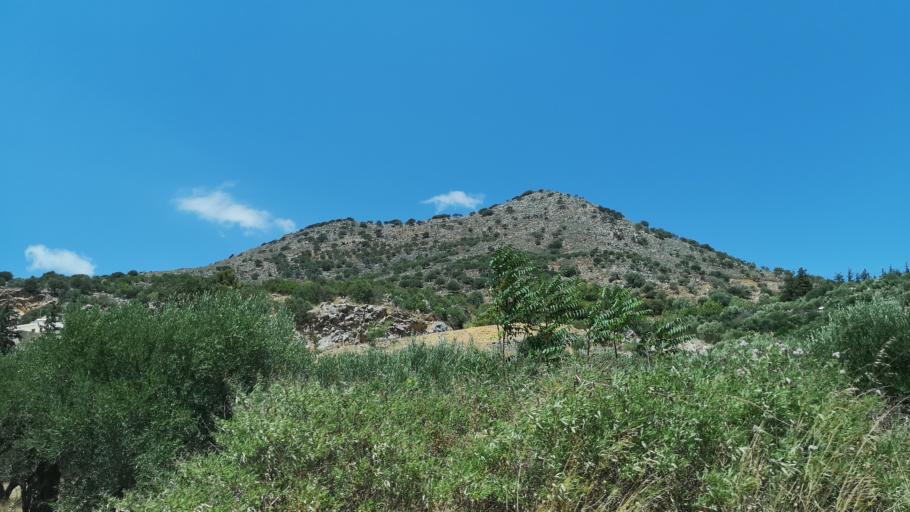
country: GR
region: Crete
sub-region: Nomos Lasithiou
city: Neapoli
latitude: 35.2486
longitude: 25.6250
